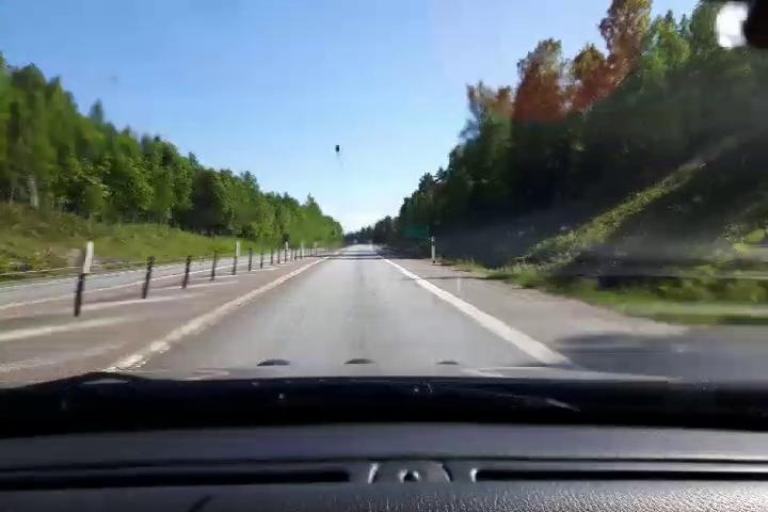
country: SE
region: Gaevleborg
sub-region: Gavle Kommun
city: Gavle
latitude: 60.7005
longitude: 17.0855
